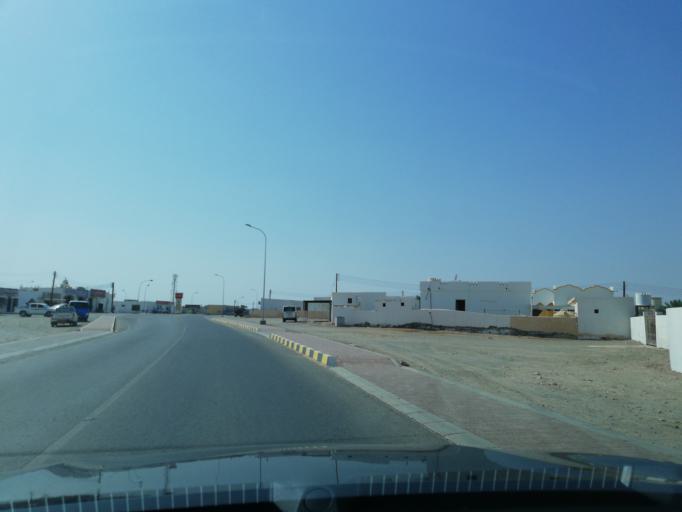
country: OM
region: Muhafazat ad Dakhiliyah
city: Adam
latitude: 22.3007
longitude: 58.0734
